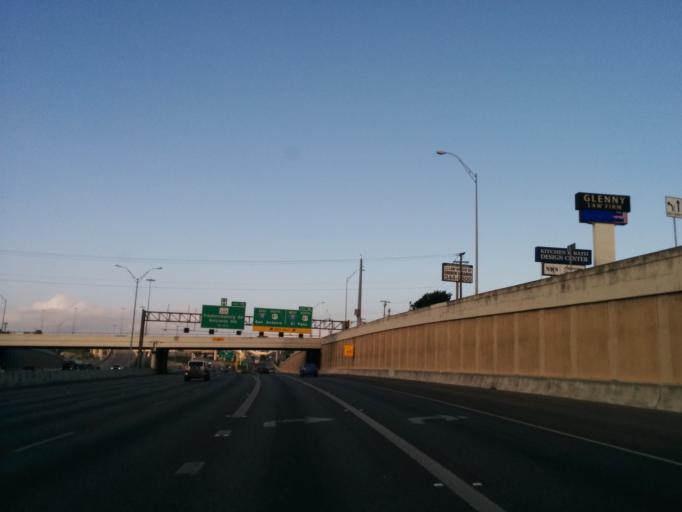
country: US
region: Texas
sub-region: Bexar County
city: Balcones Heights
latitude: 29.5084
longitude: -98.5432
